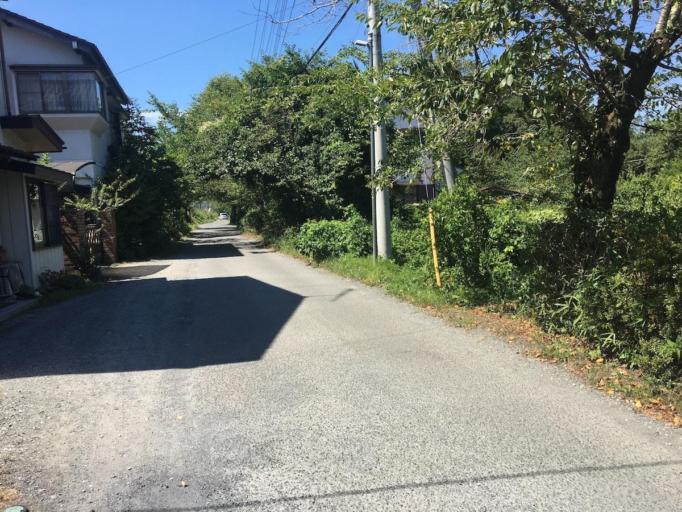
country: JP
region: Saitama
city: Yorii
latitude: 36.0914
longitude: 139.1150
